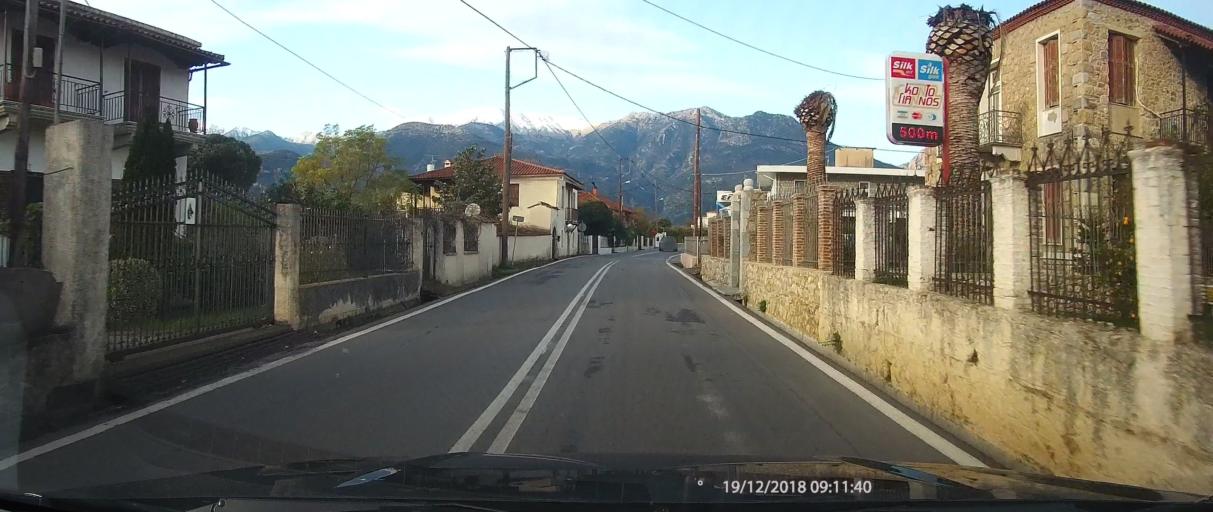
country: GR
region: Peloponnese
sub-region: Nomos Lakonias
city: Magoula
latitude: 37.0787
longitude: 22.4128
